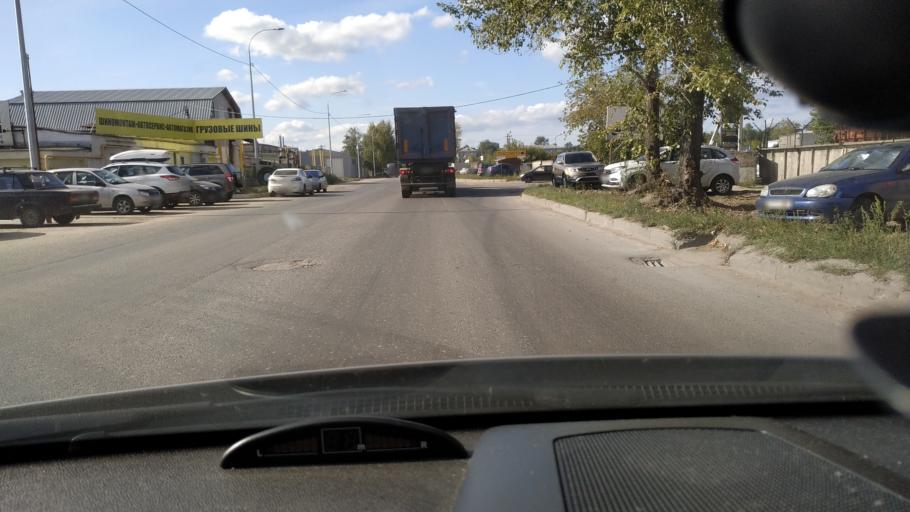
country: RU
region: Rjazan
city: Ryazan'
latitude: 54.6550
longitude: 39.6393
